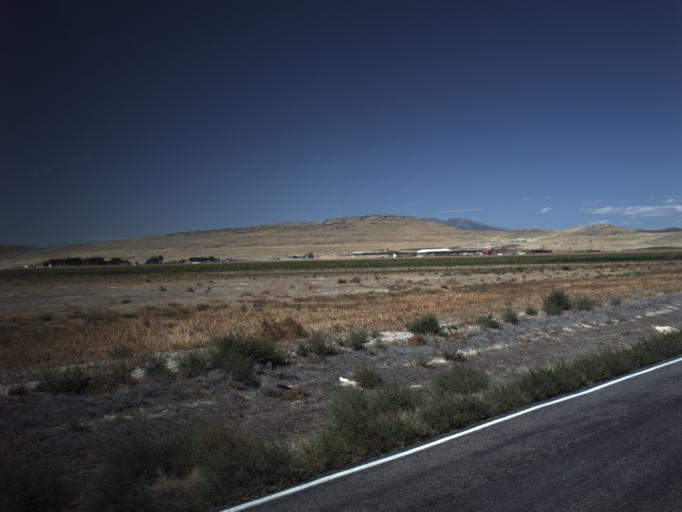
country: US
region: Utah
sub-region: Utah County
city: Genola
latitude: 40.0966
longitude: -111.9590
